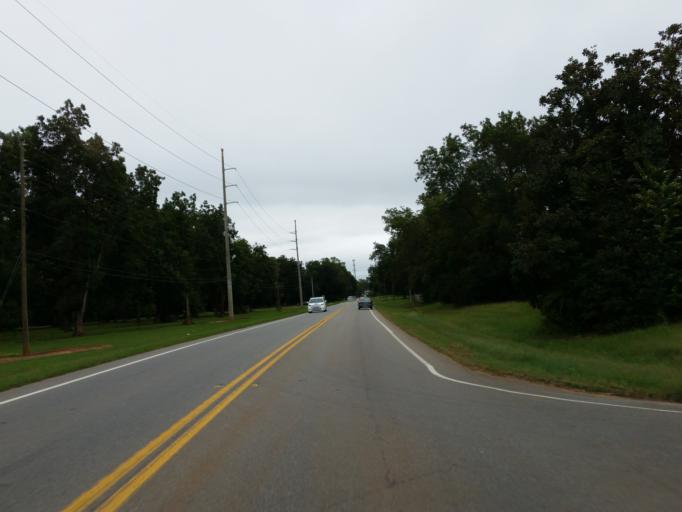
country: US
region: Georgia
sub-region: Peach County
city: Fort Valley
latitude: 32.5692
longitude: -83.8877
